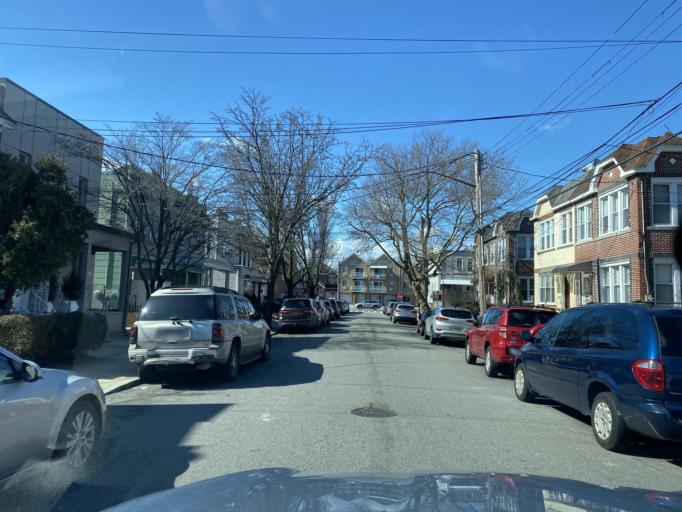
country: US
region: New York
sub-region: Kings County
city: East New York
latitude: 40.7121
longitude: -73.8782
